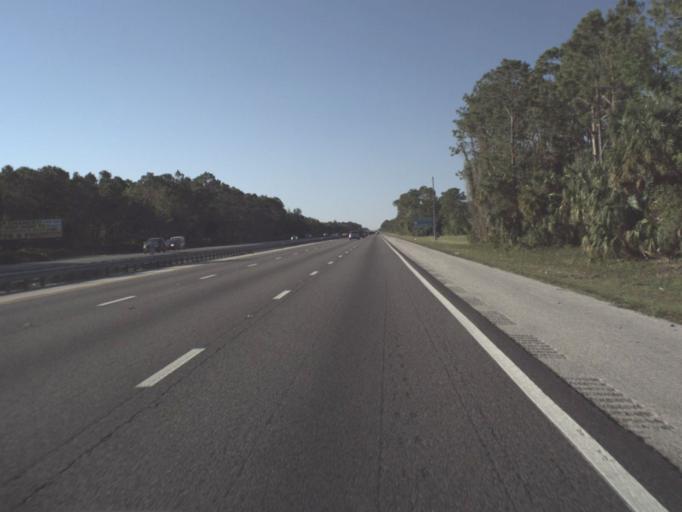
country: US
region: Florida
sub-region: Flagler County
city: Flagler Beach
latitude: 29.4463
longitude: -81.1724
